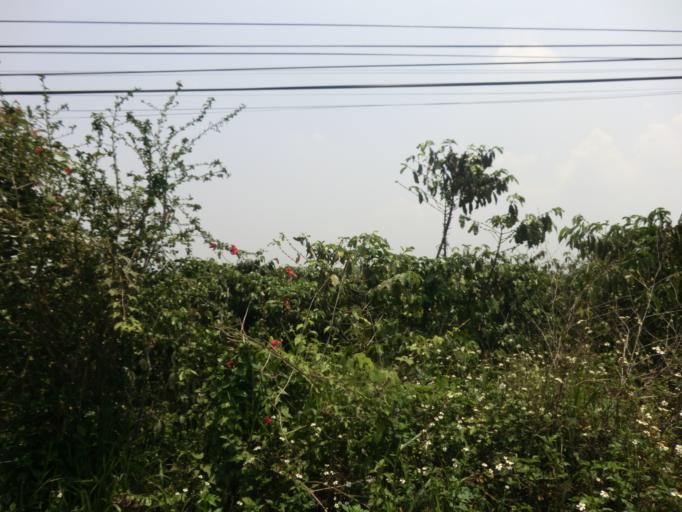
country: VN
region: Lam Dong
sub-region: Thanh Pho Bao Loc
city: Bao Loc
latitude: 11.5808
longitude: 107.8031
